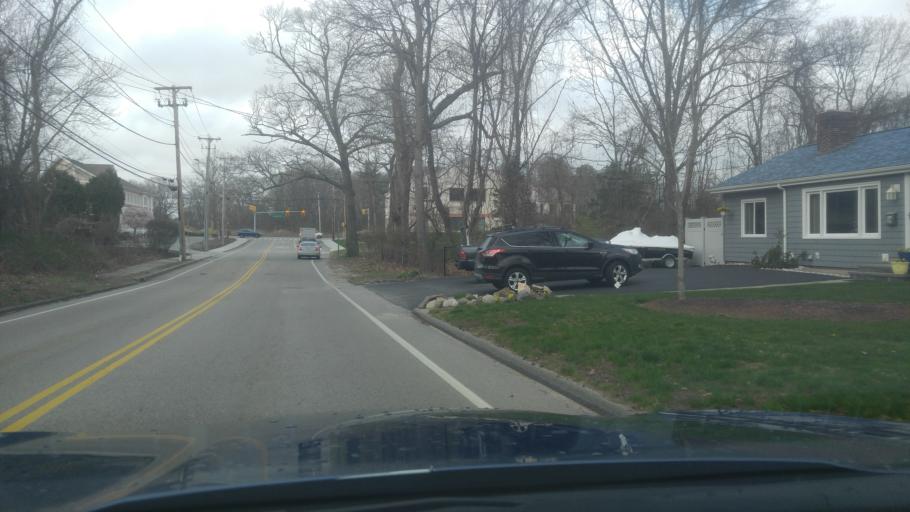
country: US
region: Rhode Island
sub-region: Kent County
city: East Greenwich
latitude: 41.6965
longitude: -71.4679
